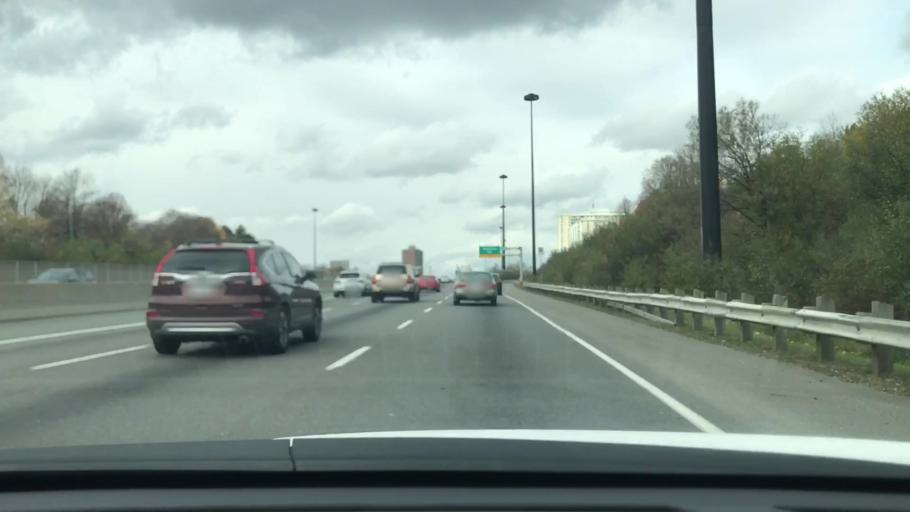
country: CA
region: Ontario
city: Willowdale
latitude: 43.7544
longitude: -79.3342
